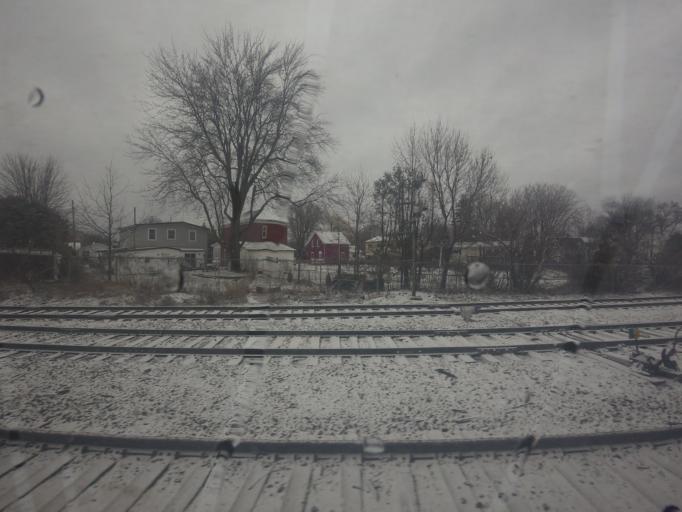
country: CA
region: Ontario
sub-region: Lanark County
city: Smiths Falls
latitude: 44.9077
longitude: -76.0199
